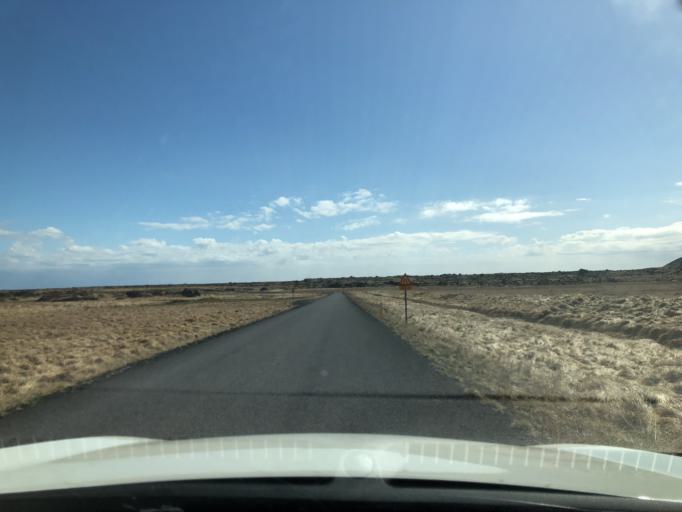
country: IS
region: West
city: Olafsvik
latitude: 64.8310
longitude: -23.4060
